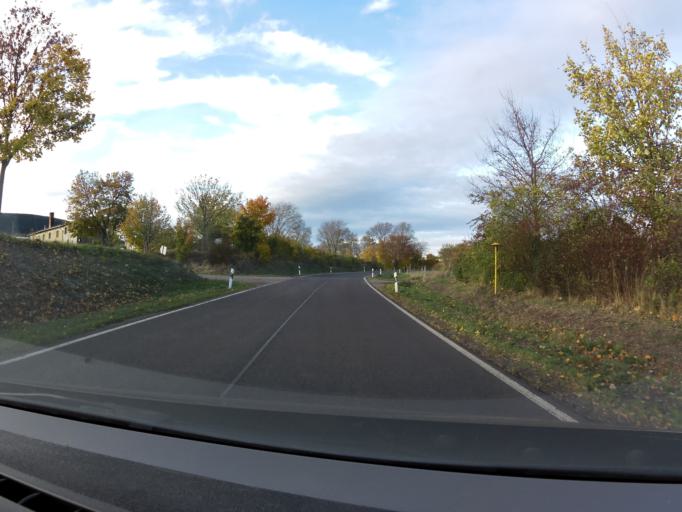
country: DE
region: Thuringia
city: Grafenroda
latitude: 50.7596
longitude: 10.7953
